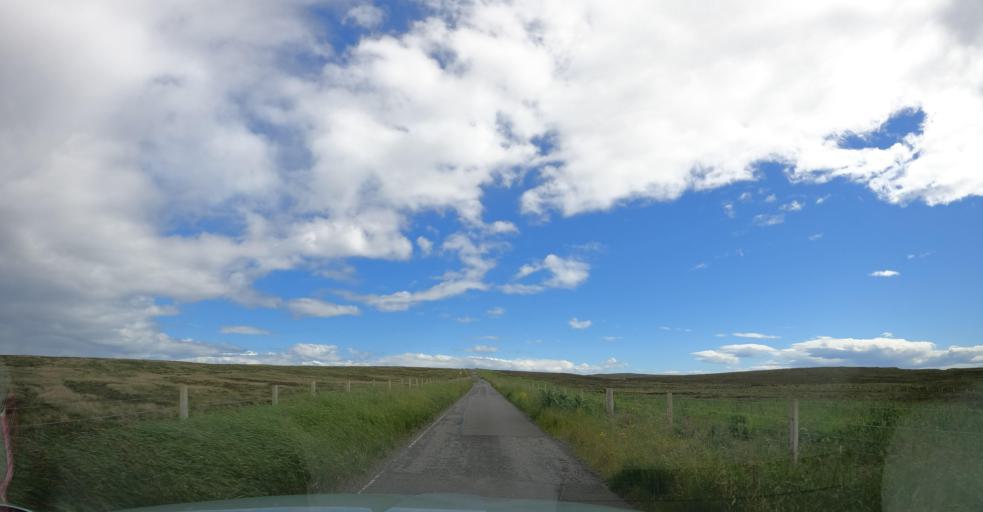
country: GB
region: Scotland
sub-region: Eilean Siar
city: Stornoway
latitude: 58.2077
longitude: -6.2500
